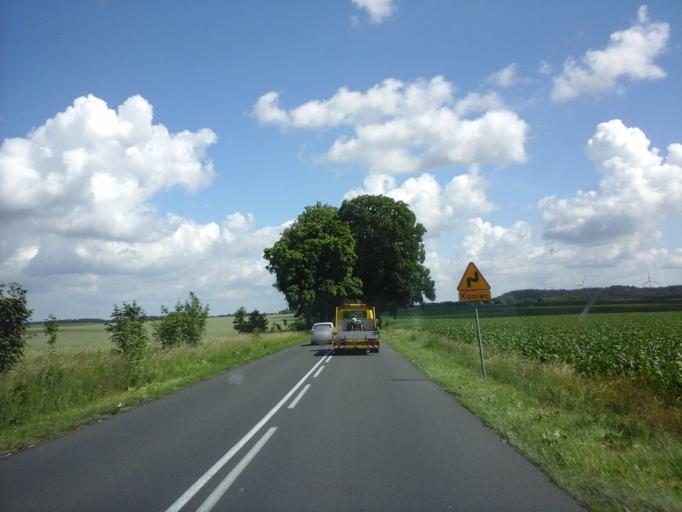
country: PL
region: West Pomeranian Voivodeship
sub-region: Powiat lobeski
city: Lobez
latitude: 53.6793
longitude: 15.6762
